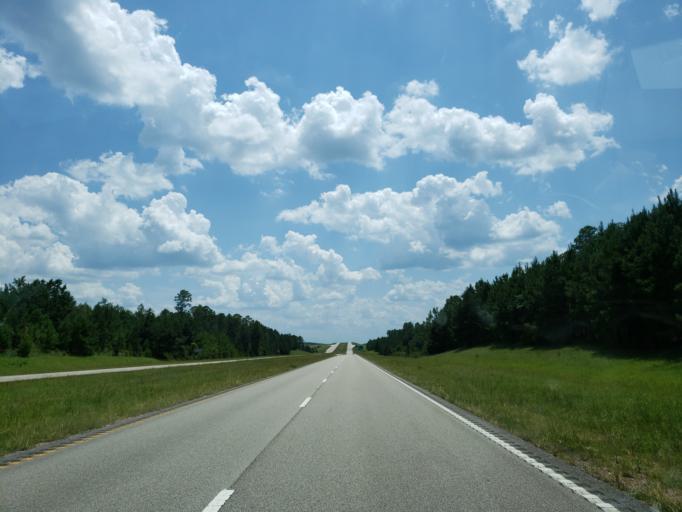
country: US
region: Mississippi
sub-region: Greene County
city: Leakesville
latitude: 31.1404
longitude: -88.5046
